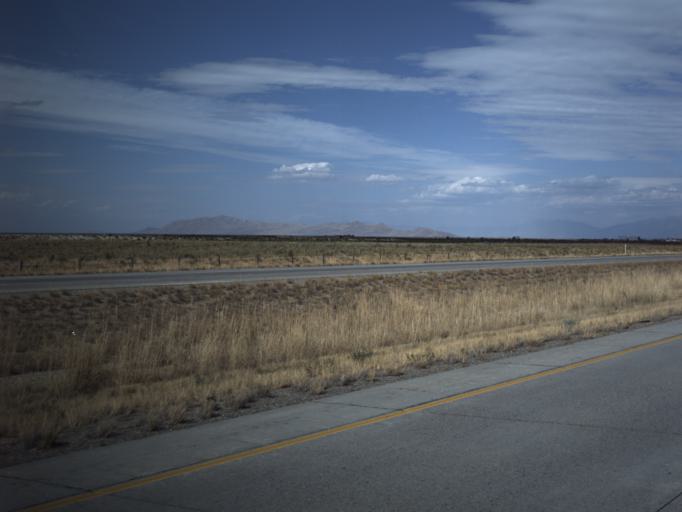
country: US
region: Utah
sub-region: Tooele County
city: Stansbury park
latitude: 40.6750
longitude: -112.2871
